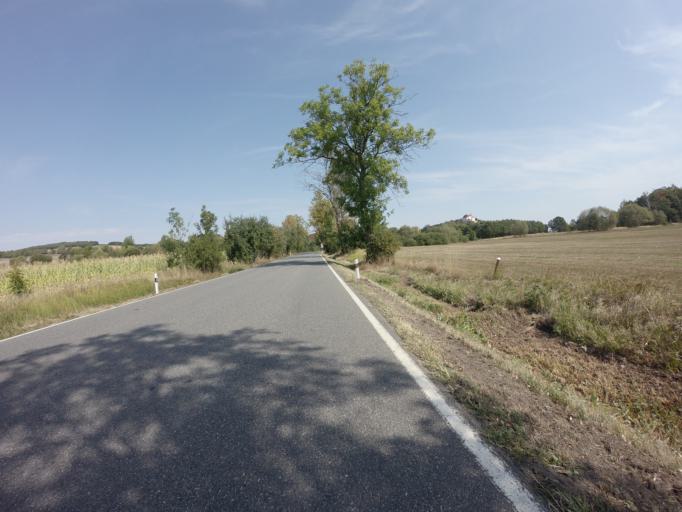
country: CZ
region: Central Bohemia
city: Sedlcany
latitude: 49.6097
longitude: 14.3846
